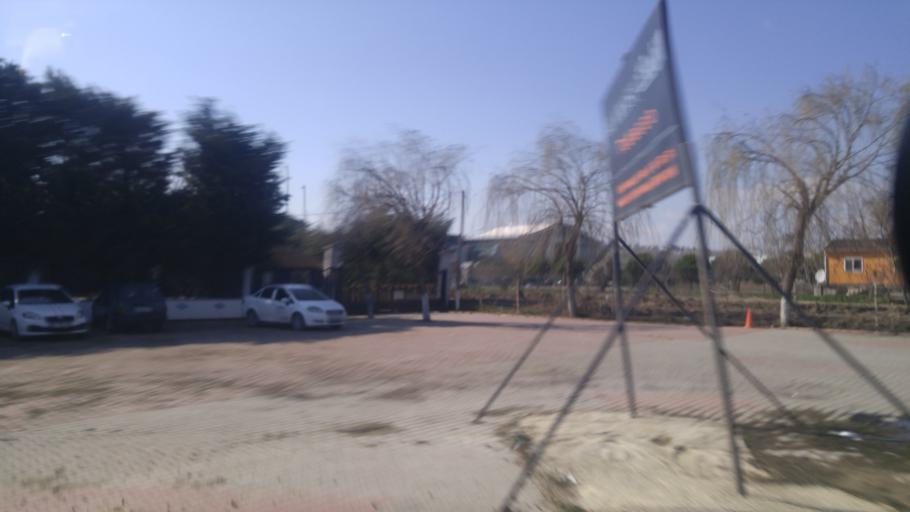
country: TR
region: Istanbul
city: Canta
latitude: 41.0755
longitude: 28.1061
